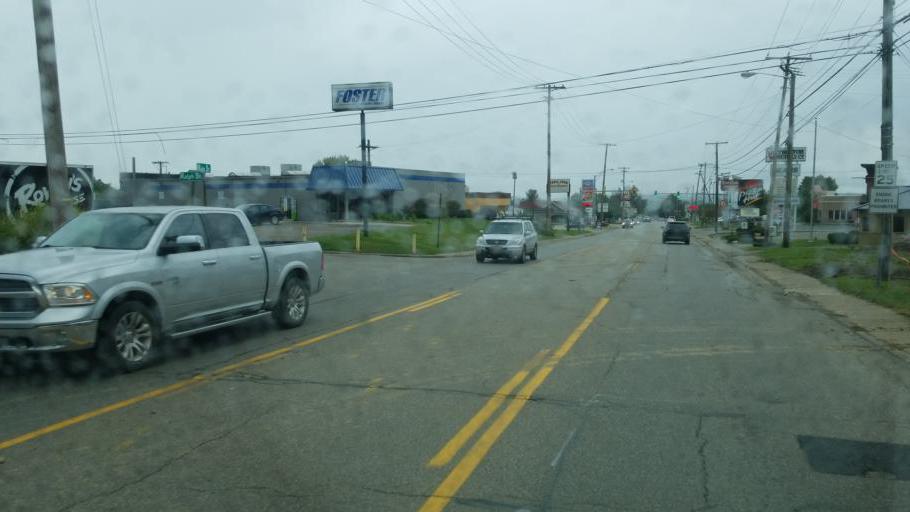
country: US
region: Ohio
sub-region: Jackson County
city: Jackson
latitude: 39.0400
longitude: -82.6281
